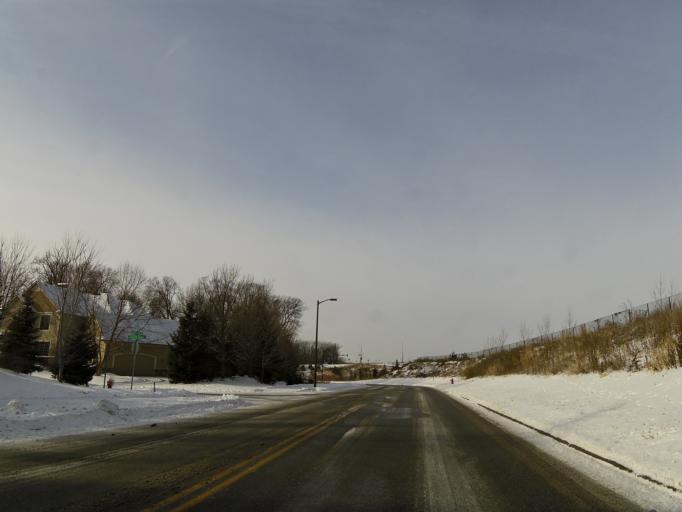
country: US
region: Minnesota
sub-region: Hennepin County
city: Eden Prairie
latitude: 44.8496
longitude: -93.4996
